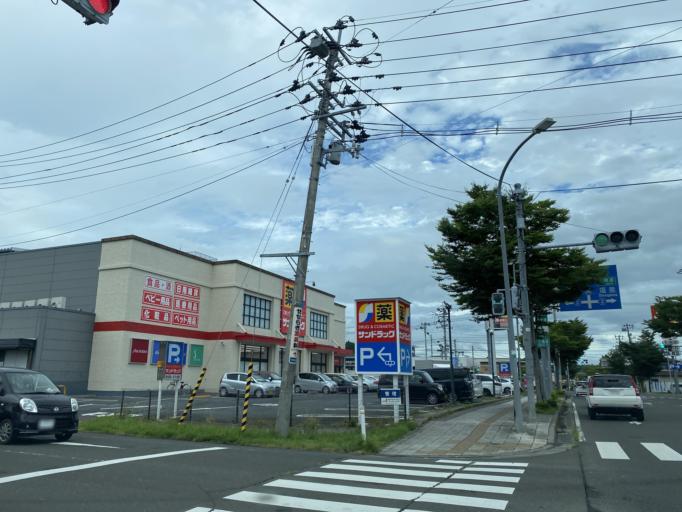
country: JP
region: Miyagi
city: Rifu
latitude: 38.3287
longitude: 140.9722
